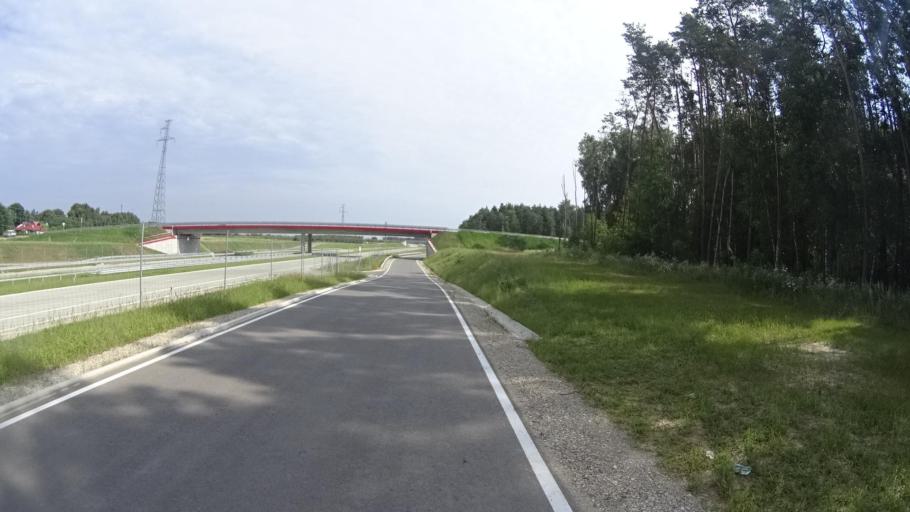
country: PL
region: Masovian Voivodeship
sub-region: Powiat piaseczynski
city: Tarczyn
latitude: 51.9651
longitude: 20.8587
